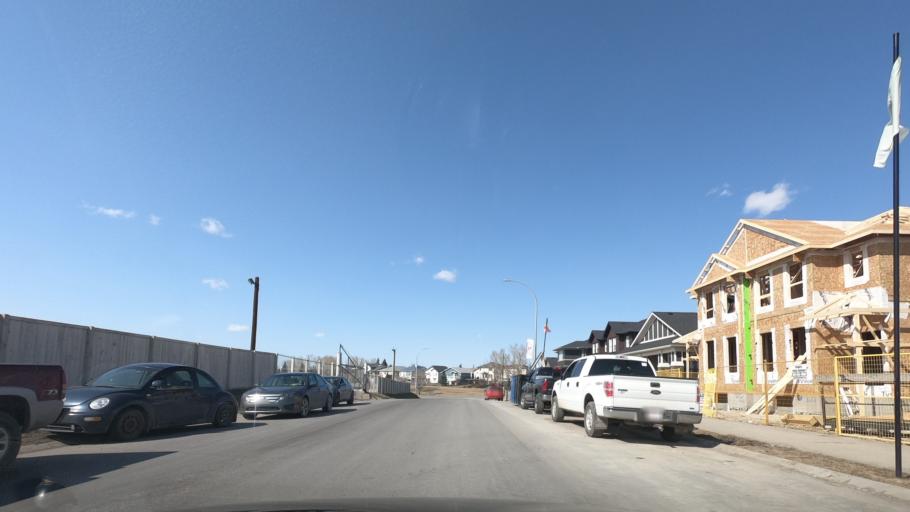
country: CA
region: Alberta
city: Airdrie
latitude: 51.2696
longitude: -113.9816
